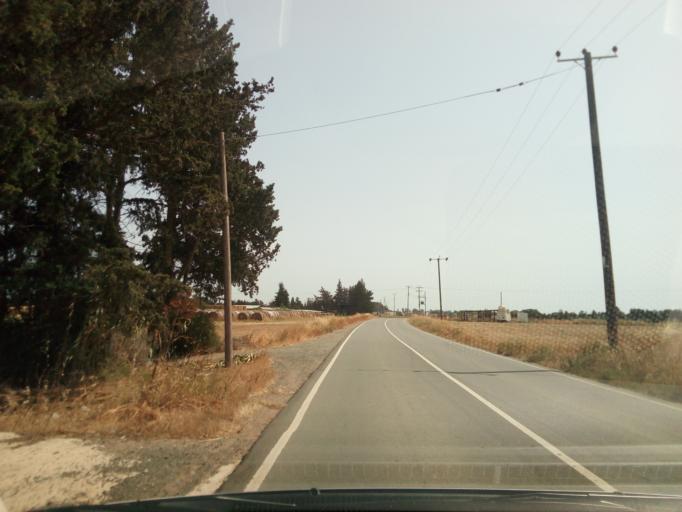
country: CY
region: Larnaka
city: Meneou
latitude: 34.8526
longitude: 33.5953
